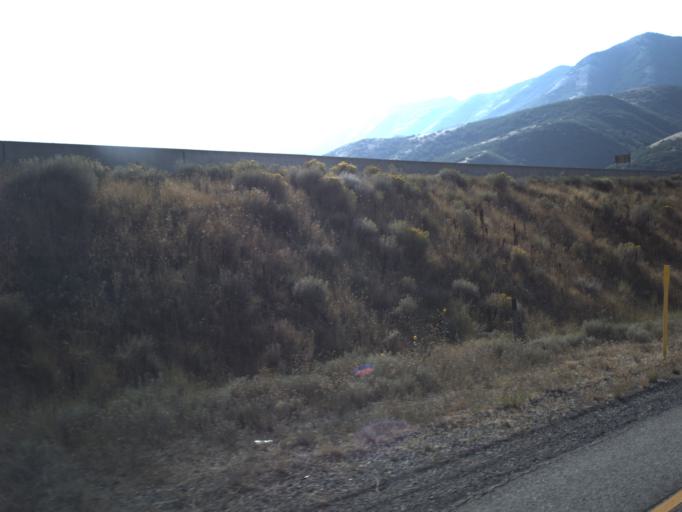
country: US
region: Utah
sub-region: Summit County
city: Summit Park
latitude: 40.7512
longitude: -111.7108
